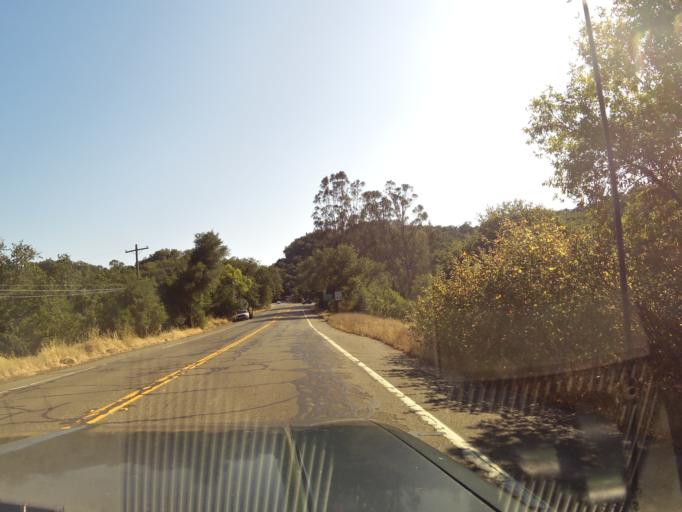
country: US
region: California
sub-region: Sonoma County
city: Cloverdale
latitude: 38.8207
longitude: -123.0209
